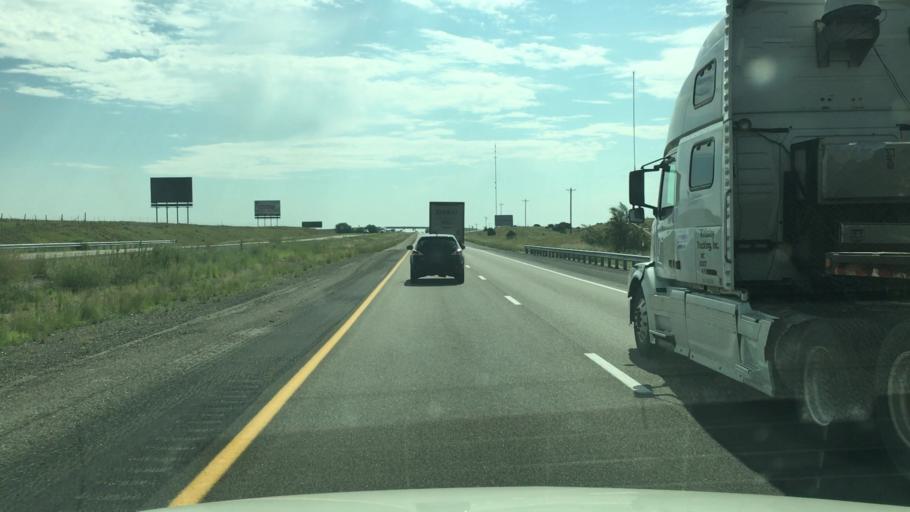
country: US
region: New Mexico
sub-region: San Miguel County
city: Las Vegas
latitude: 34.9920
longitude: -105.3058
